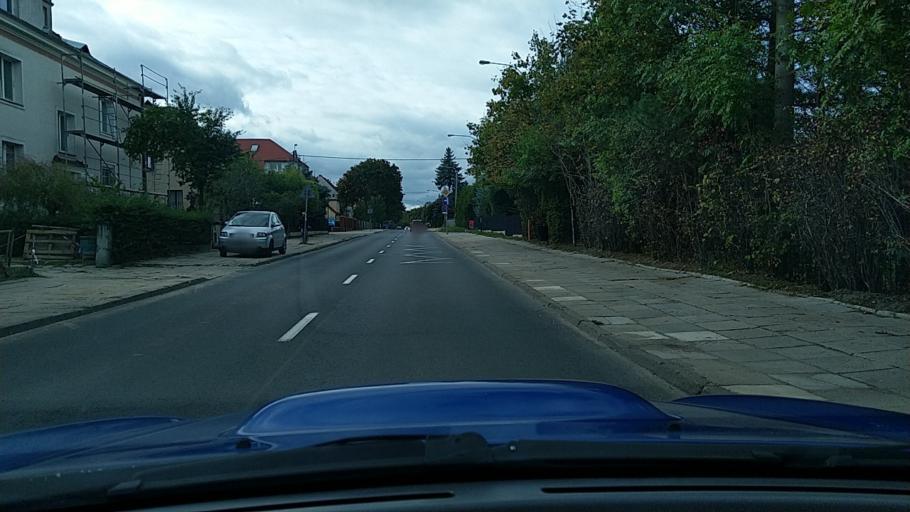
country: PL
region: Warmian-Masurian Voivodeship
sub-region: Olsztyn
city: Kortowo
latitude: 53.7704
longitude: 20.4626
